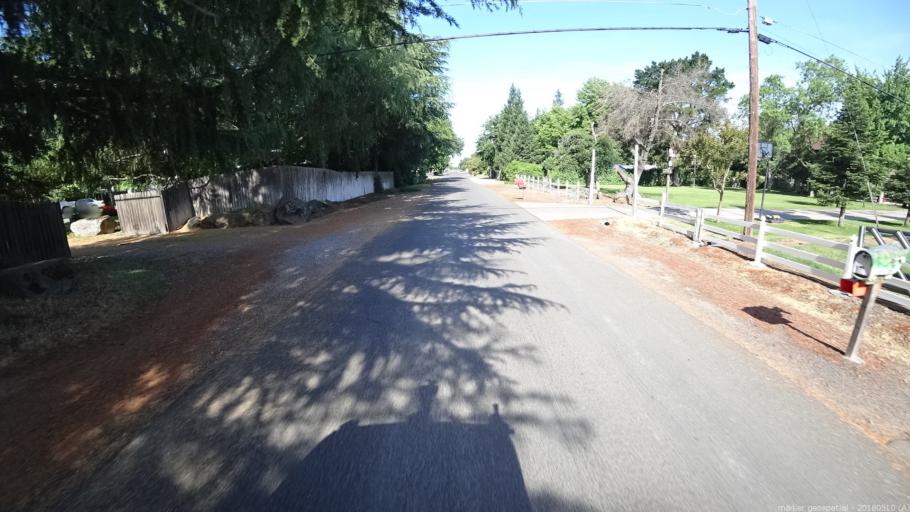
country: US
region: California
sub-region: Sacramento County
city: Rio Linda
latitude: 38.6628
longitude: -121.4799
